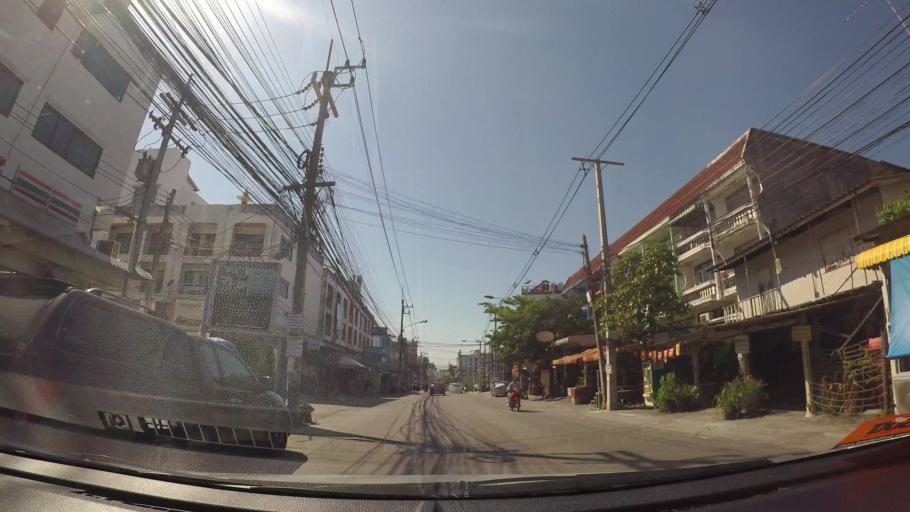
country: TH
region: Chon Buri
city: Si Racha
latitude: 13.1571
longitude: 100.9320
